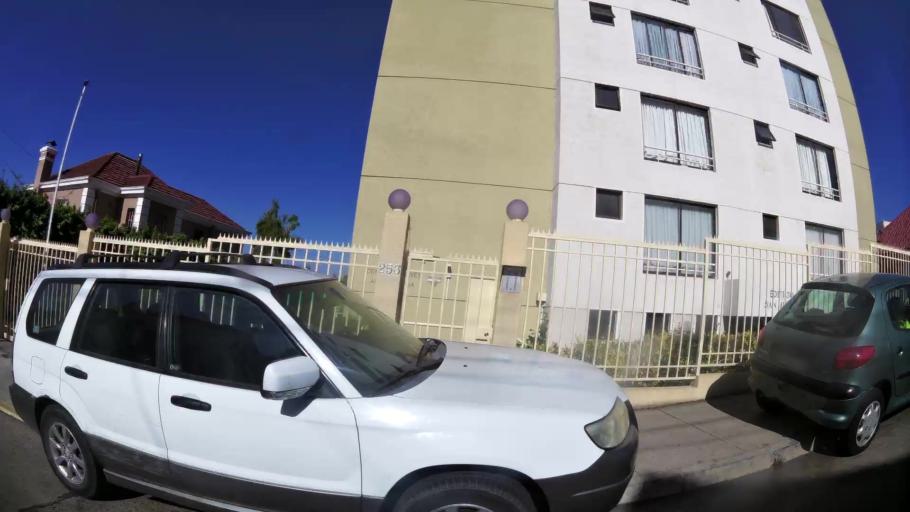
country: CL
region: Valparaiso
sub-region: Provincia de Valparaiso
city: Vina del Mar
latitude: -33.0281
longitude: -71.5604
